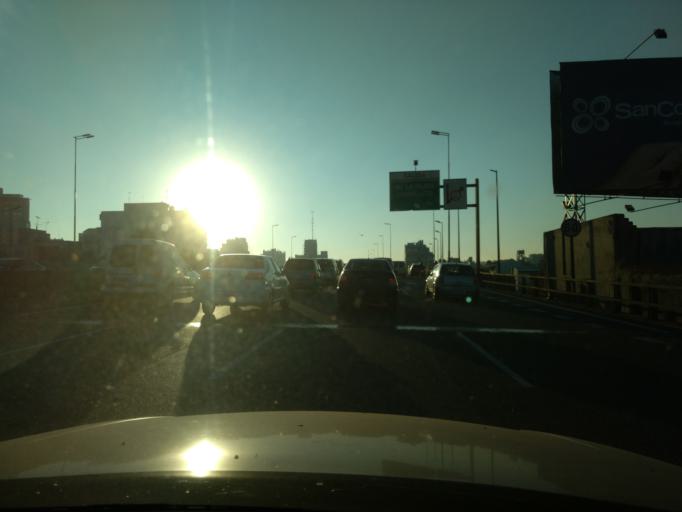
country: AR
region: Buenos Aires F.D.
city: Villa Santa Rita
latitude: -34.6300
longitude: -58.4339
